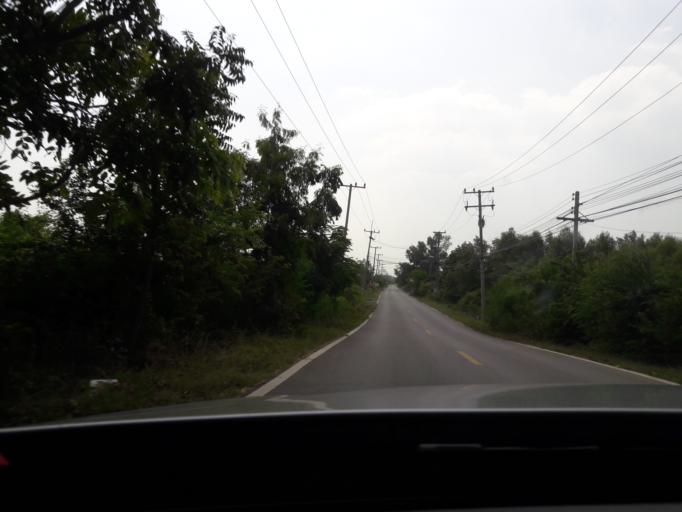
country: TH
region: Samut Songkhram
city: Amphawa
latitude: 13.3318
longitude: 99.9583
